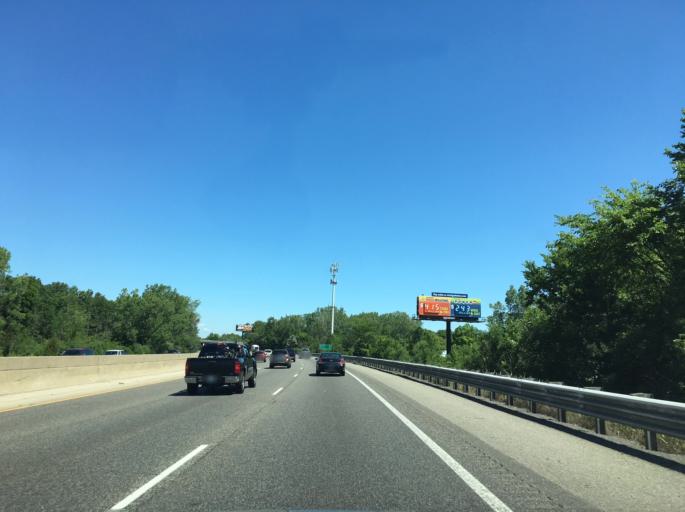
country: US
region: Michigan
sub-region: Genesee County
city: Flint
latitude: 43.0128
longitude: -83.7475
